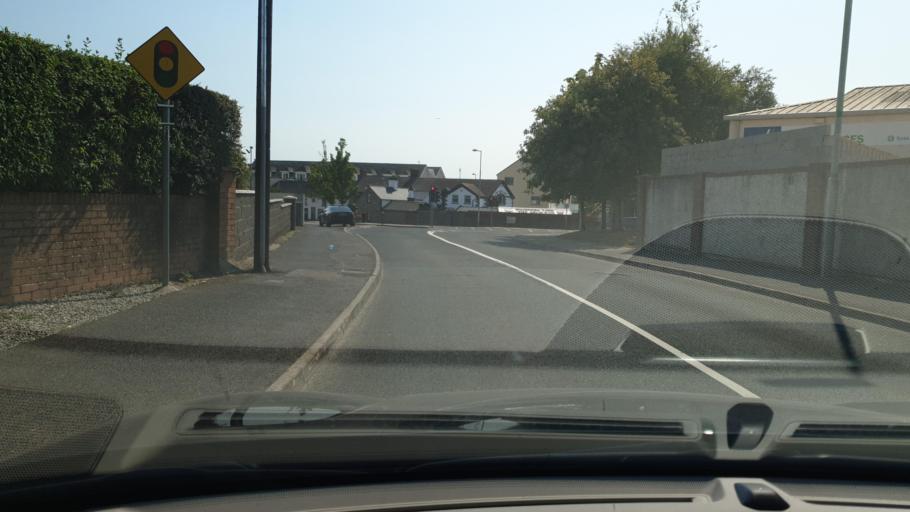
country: IE
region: Leinster
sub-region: An Mhi
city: Dunshaughlin
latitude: 53.5149
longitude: -6.5411
